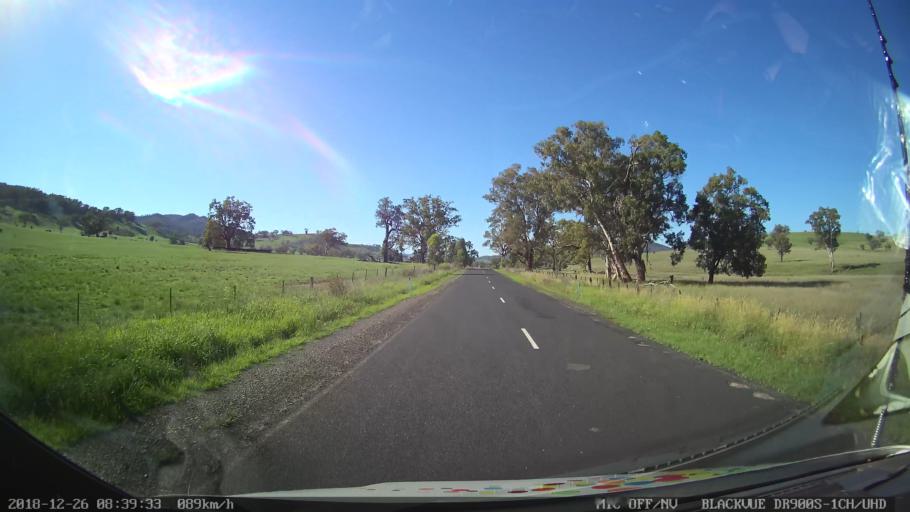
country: AU
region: New South Wales
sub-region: Mid-Western Regional
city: Kandos
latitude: -32.4549
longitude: 150.0756
